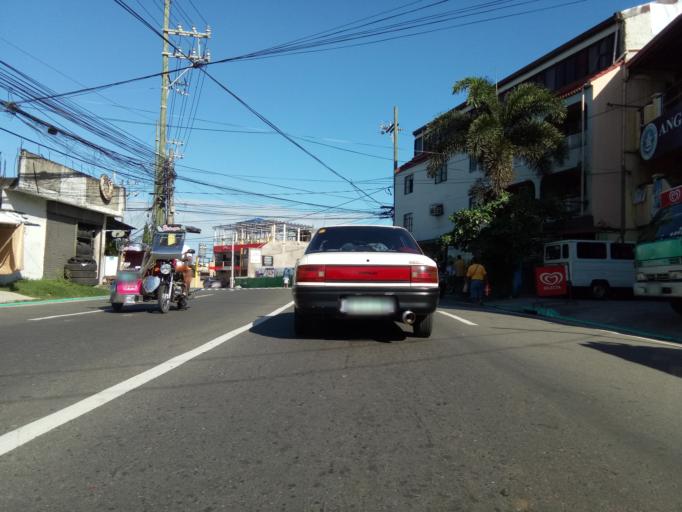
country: PH
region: Calabarzon
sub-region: Province of Cavite
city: Dasmarinas
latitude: 14.3514
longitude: 120.9445
